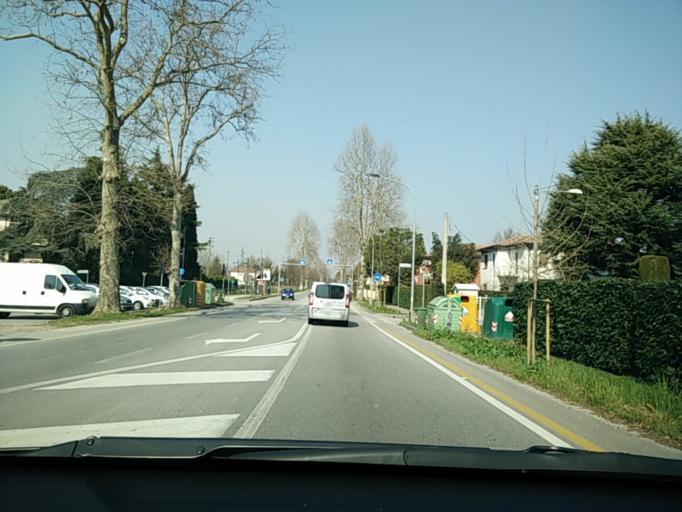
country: IT
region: Veneto
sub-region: Provincia di Venezia
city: Zelarino
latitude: 45.5230
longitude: 12.2387
